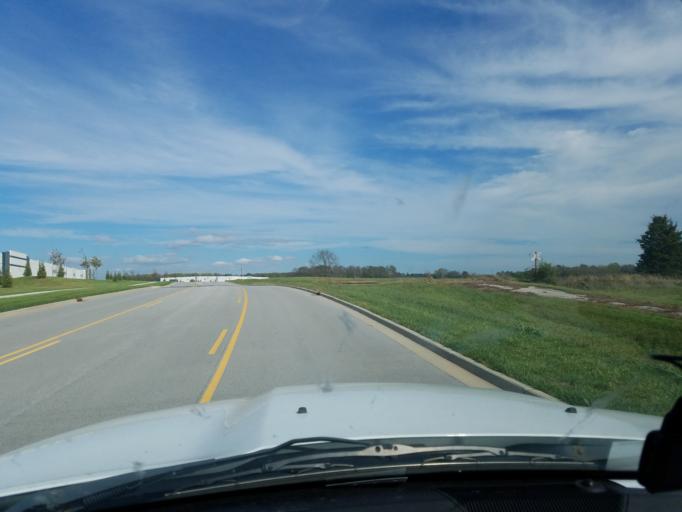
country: US
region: Indiana
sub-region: Clark County
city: Charlestown
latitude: 38.3838
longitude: -85.6775
